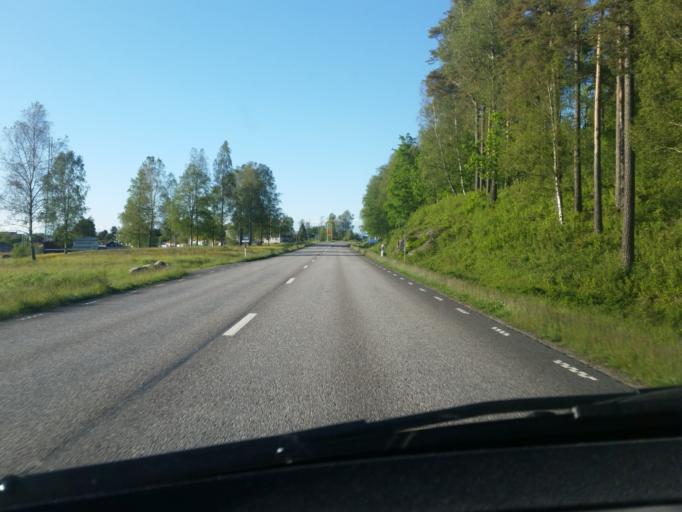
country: SE
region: Vaestra Goetaland
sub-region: Fargelanda Kommun
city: Faergelanda
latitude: 58.5595
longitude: 11.9956
